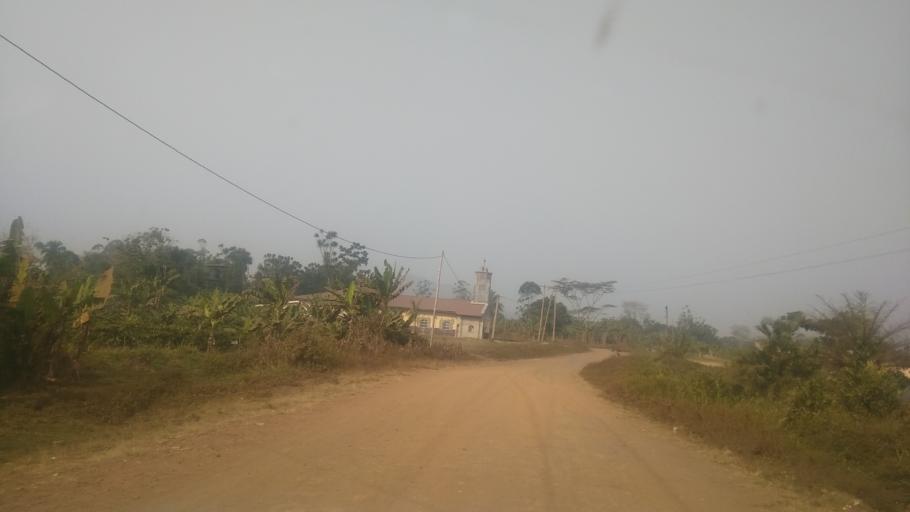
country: CM
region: Littoral
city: Melong
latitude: 5.1295
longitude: 9.8196
